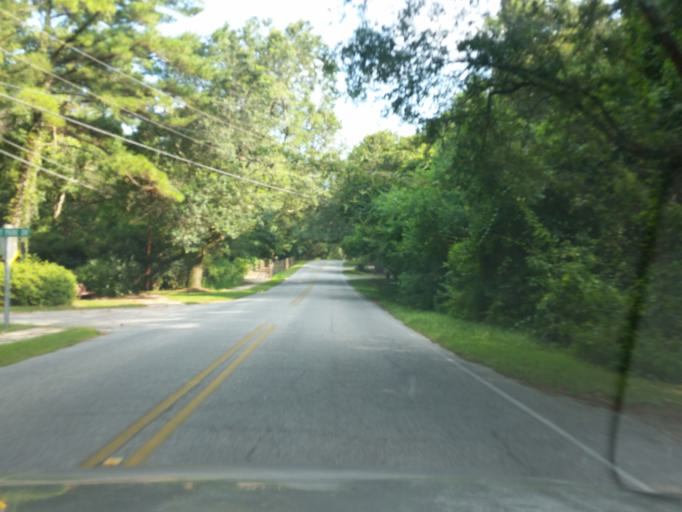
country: US
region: Alabama
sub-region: Baldwin County
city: Daphne
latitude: 30.5637
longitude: -87.9003
